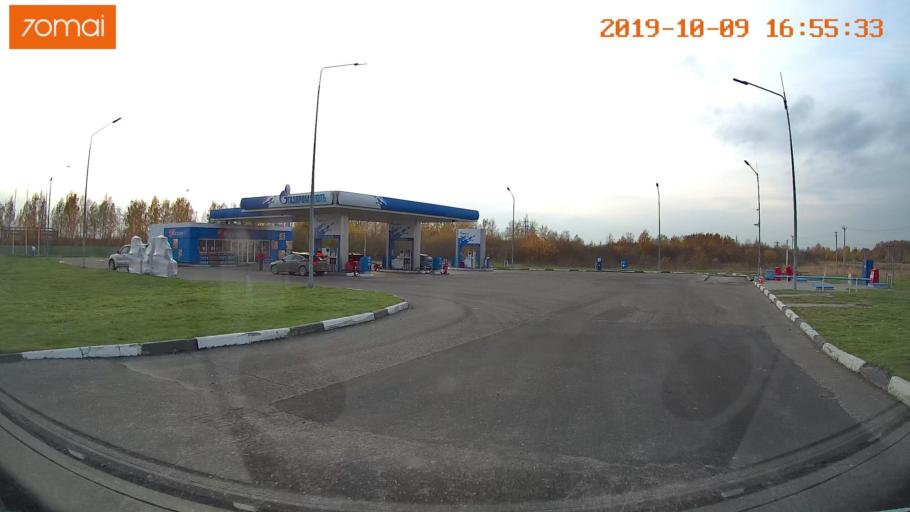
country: RU
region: Ivanovo
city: Privolzhsk
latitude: 57.3673
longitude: 41.2730
